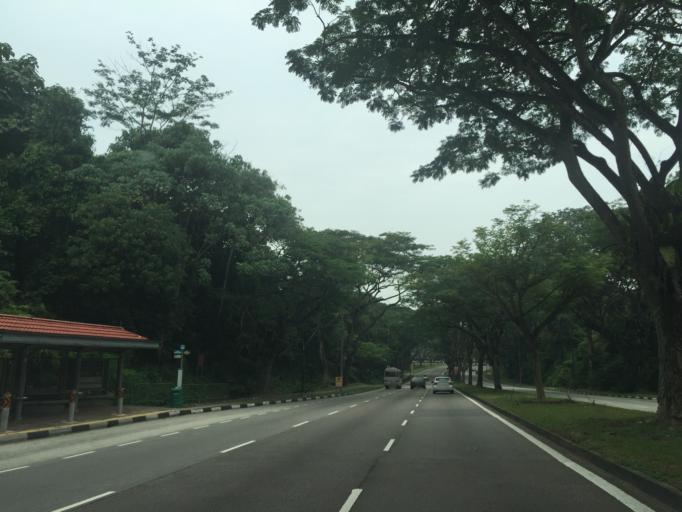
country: SG
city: Singapore
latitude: 1.3853
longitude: 103.8229
